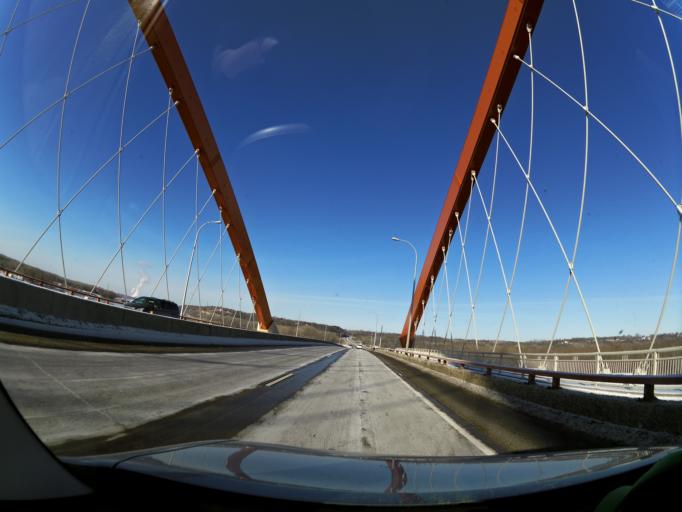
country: US
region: Minnesota
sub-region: Dakota County
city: Hastings
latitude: 44.7462
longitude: -92.8530
